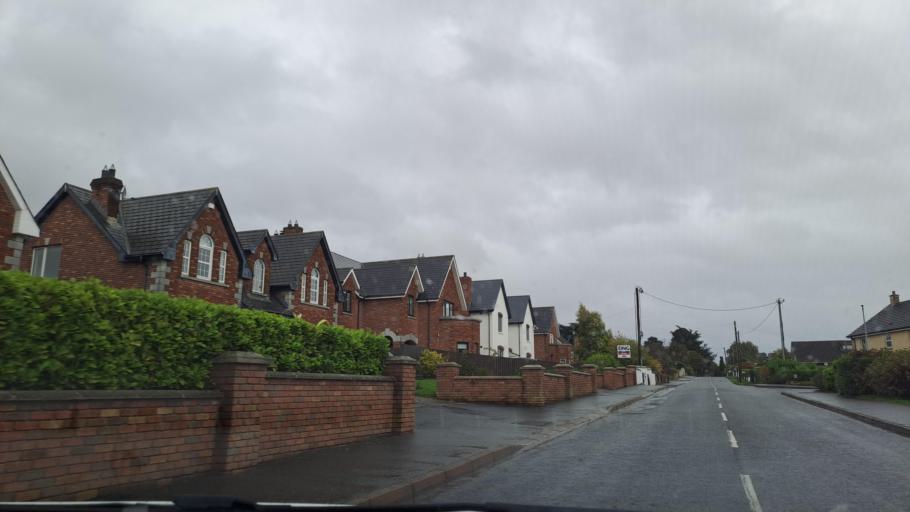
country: IE
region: Leinster
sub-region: Lu
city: Blackrock
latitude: 53.9633
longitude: -6.3864
